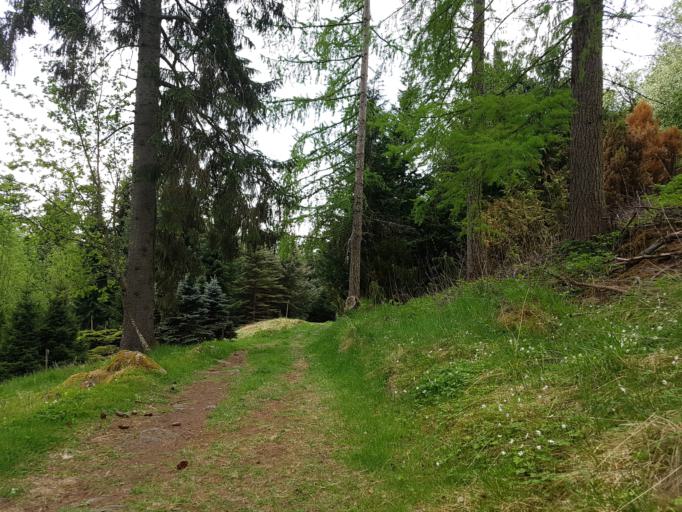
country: NO
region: Nord-Trondelag
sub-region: Levanger
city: Levanger
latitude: 63.7415
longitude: 11.2663
